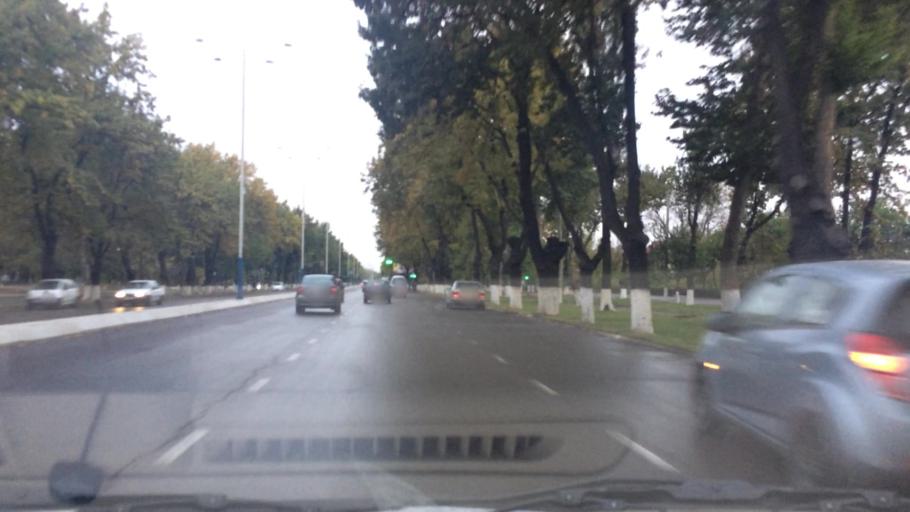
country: UZ
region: Toshkent Shahri
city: Tashkent
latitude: 41.2661
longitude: 69.1996
